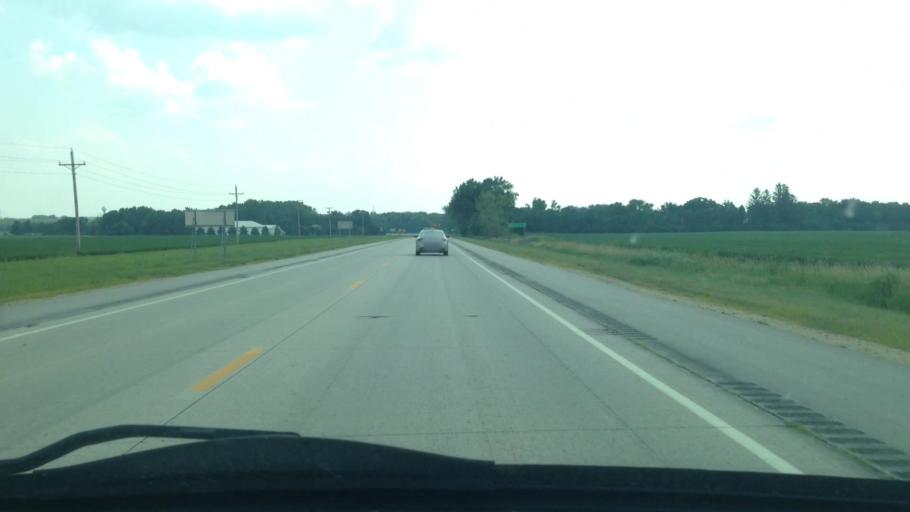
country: US
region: Minnesota
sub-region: Fillmore County
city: Spring Valley
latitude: 43.5067
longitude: -92.3694
